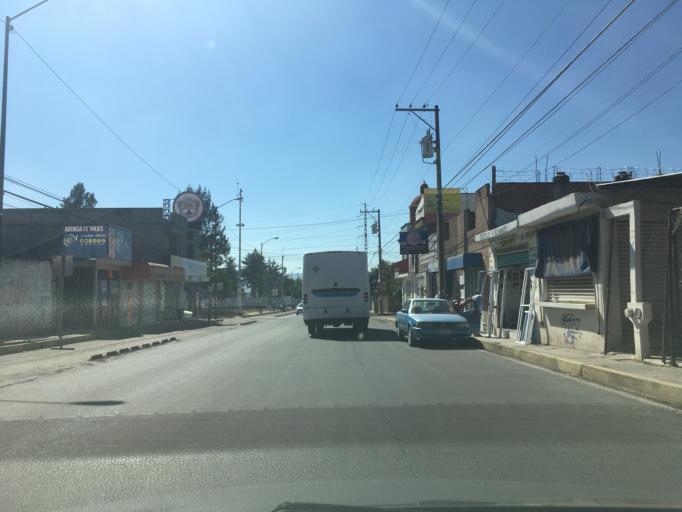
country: MX
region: Michoacan
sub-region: Morelia
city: San Antonio
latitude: 19.6930
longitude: -101.2504
